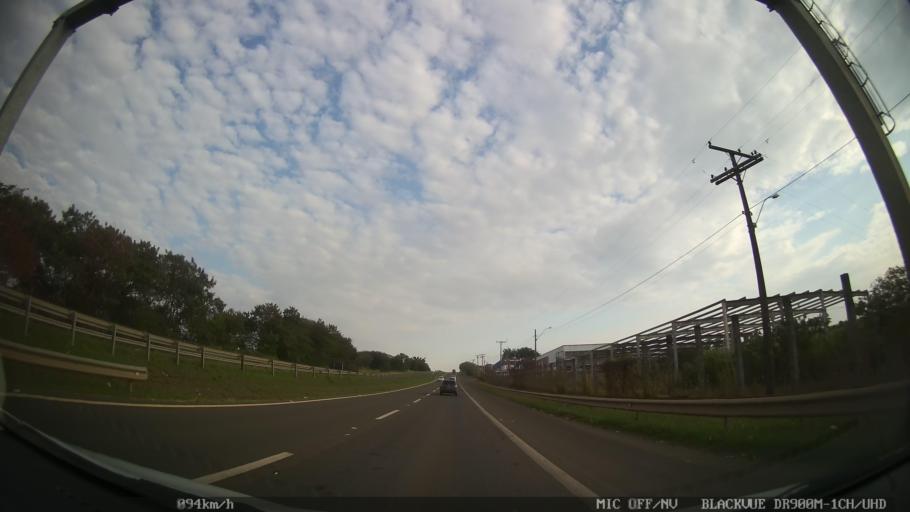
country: BR
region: Sao Paulo
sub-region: Cosmopolis
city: Cosmopolis
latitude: -22.6277
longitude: -47.2033
